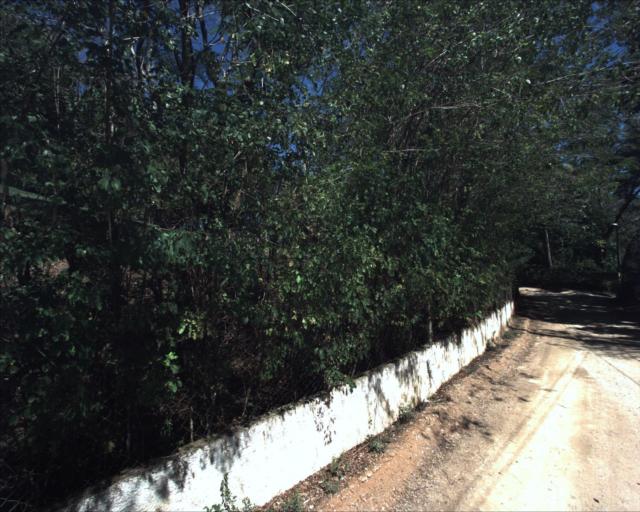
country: BR
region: Sao Paulo
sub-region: Sorocaba
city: Sorocaba
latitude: -23.4981
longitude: -47.3956
